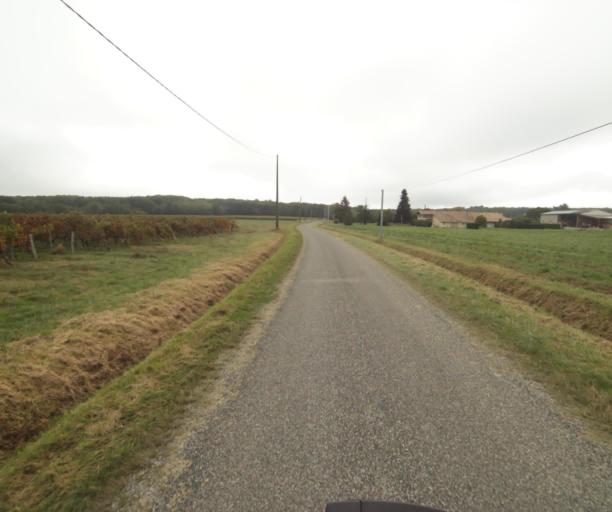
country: FR
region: Midi-Pyrenees
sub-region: Departement du Tarn-et-Garonne
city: Campsas
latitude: 43.8785
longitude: 1.3604
